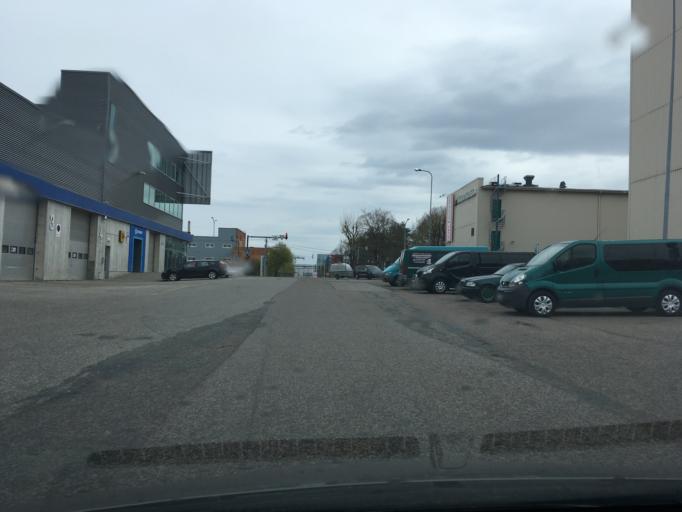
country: EE
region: Harju
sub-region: Tallinna linn
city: Tallinn
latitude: 59.4259
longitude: 24.8181
